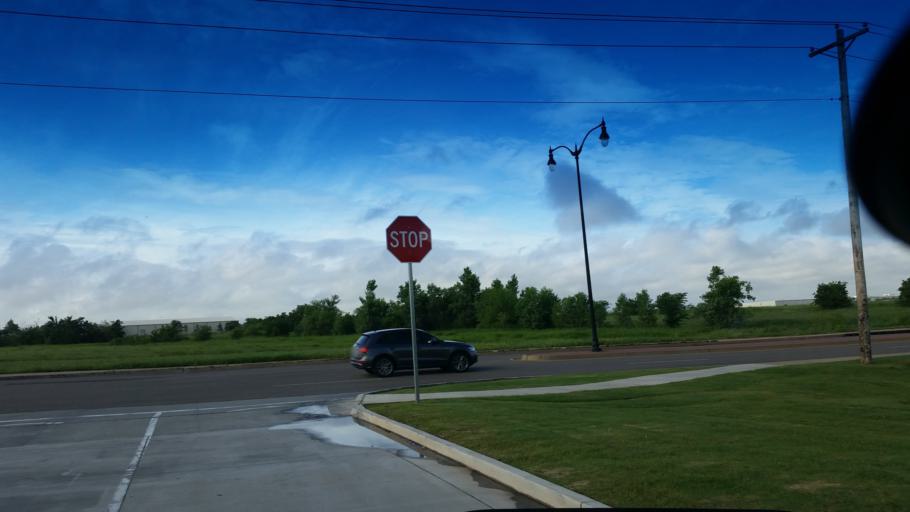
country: US
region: Oklahoma
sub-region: Oklahoma County
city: Edmond
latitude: 35.6240
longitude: -97.4983
